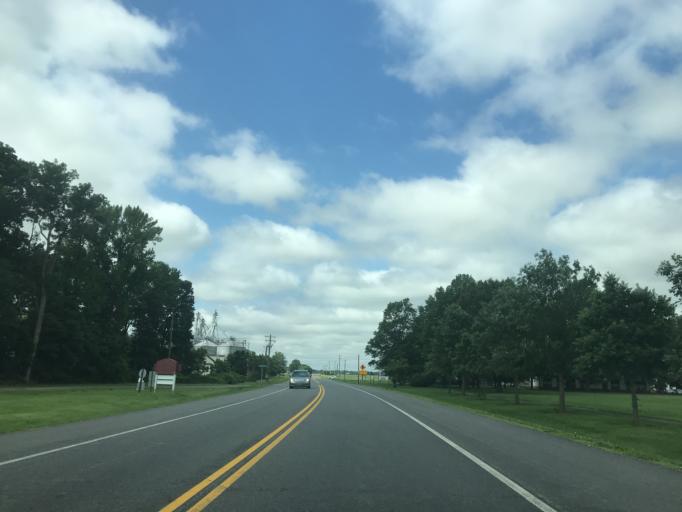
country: US
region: Maryland
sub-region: Caroline County
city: Ridgely
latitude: 38.9403
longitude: -75.8858
